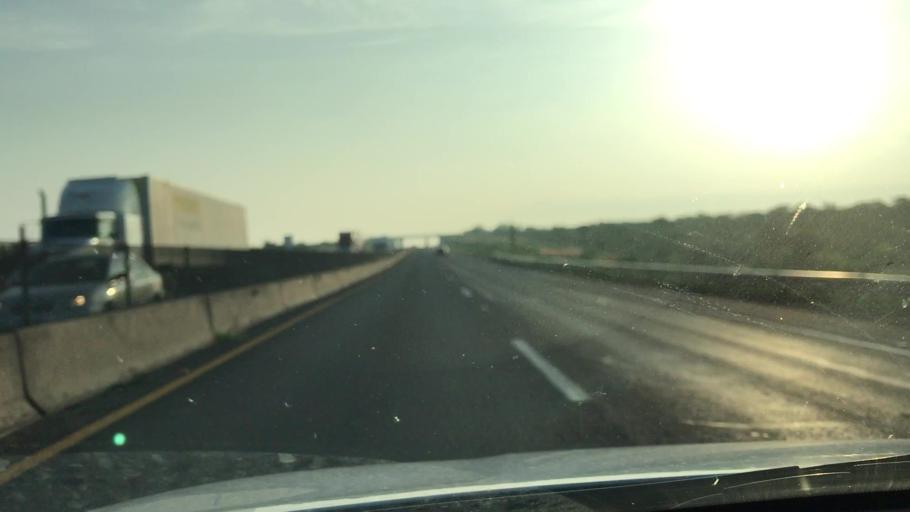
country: MX
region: Jalisco
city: Jalostotitlan
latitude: 21.0788
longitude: -102.4981
